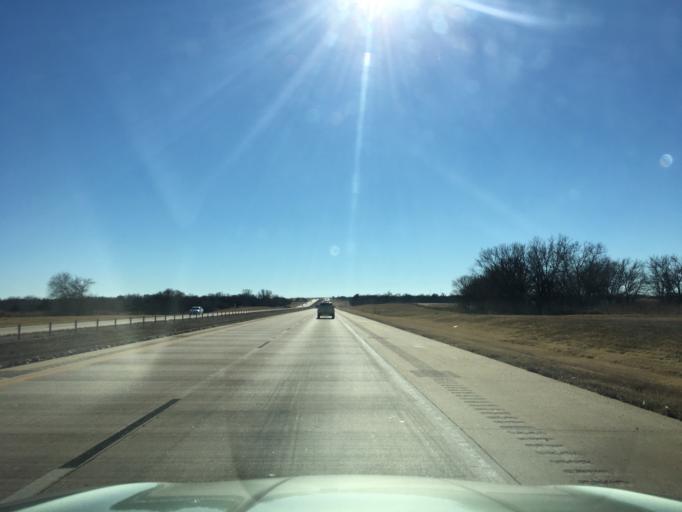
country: US
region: Oklahoma
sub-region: Noble County
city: Perry
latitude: 36.4435
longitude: -97.3271
